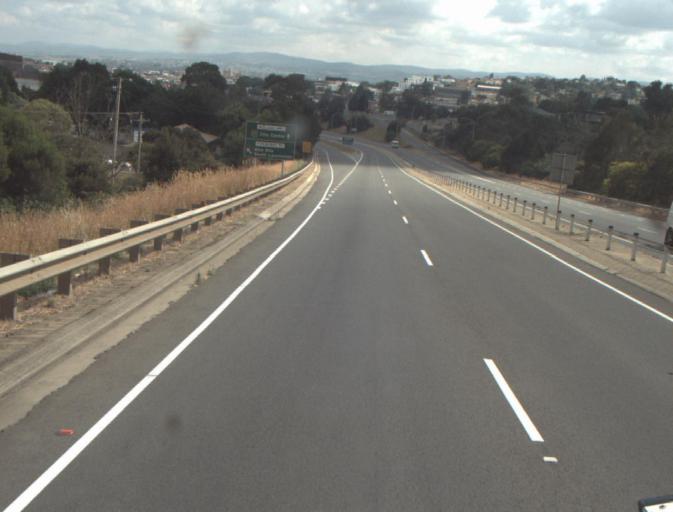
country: AU
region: Tasmania
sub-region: Launceston
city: West Launceston
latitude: -41.4588
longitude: 147.1427
